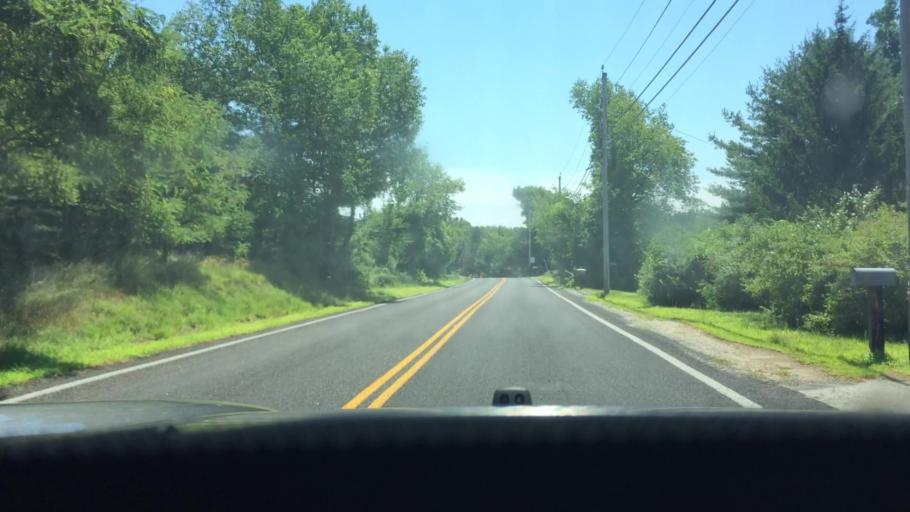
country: US
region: Rhode Island
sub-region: Providence County
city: Harrisville
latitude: 41.9751
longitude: -71.6806
